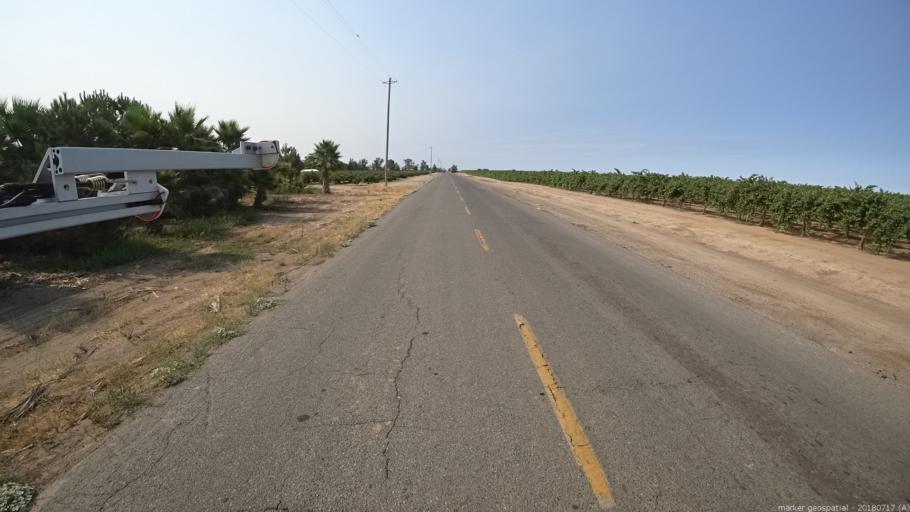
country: US
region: California
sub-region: Madera County
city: Madera Acres
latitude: 37.0671
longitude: -120.1108
